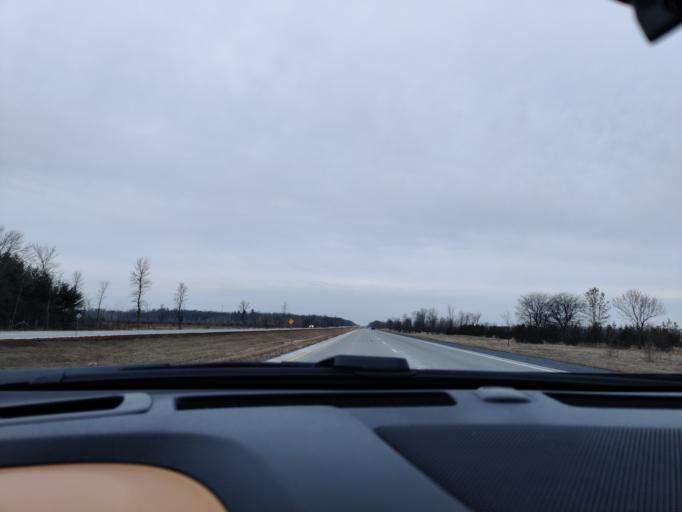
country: US
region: New York
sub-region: St. Lawrence County
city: Massena
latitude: 45.0327
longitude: -74.9438
